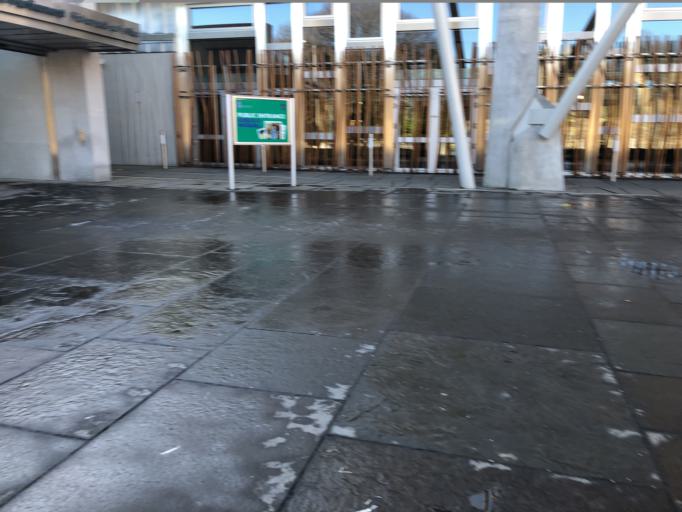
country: GB
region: Scotland
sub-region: Edinburgh
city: Edinburgh
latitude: 55.9520
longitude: -3.1740
